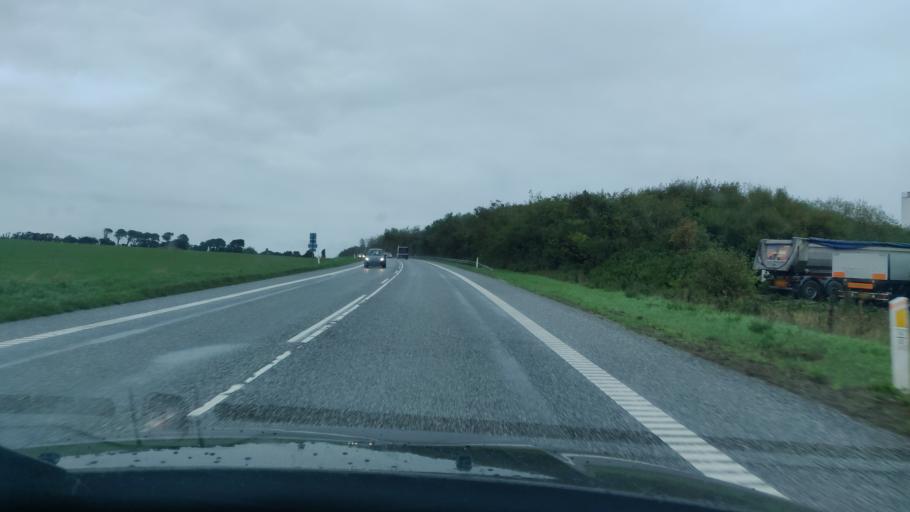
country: DK
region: North Denmark
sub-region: Thisted Kommune
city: Thisted
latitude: 56.9727
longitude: 8.7457
